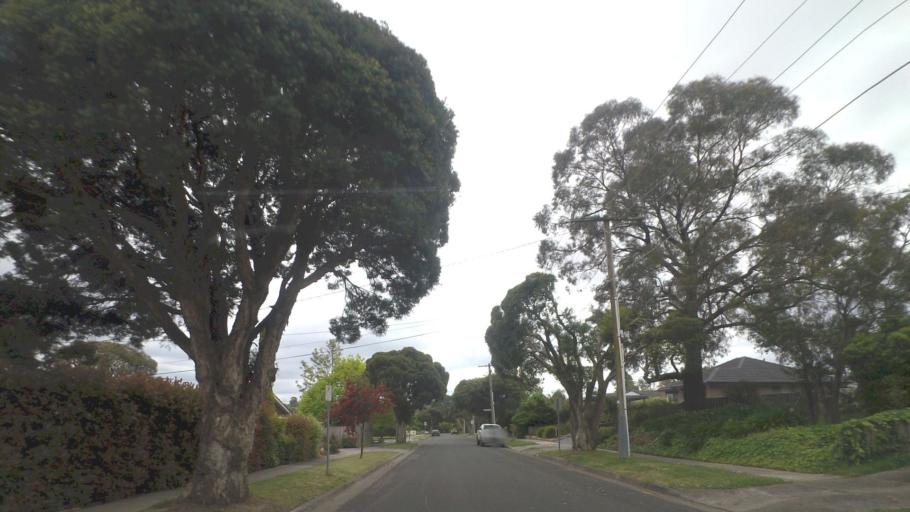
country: AU
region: Victoria
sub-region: Knox
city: Bayswater
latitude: -37.8540
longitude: 145.2615
